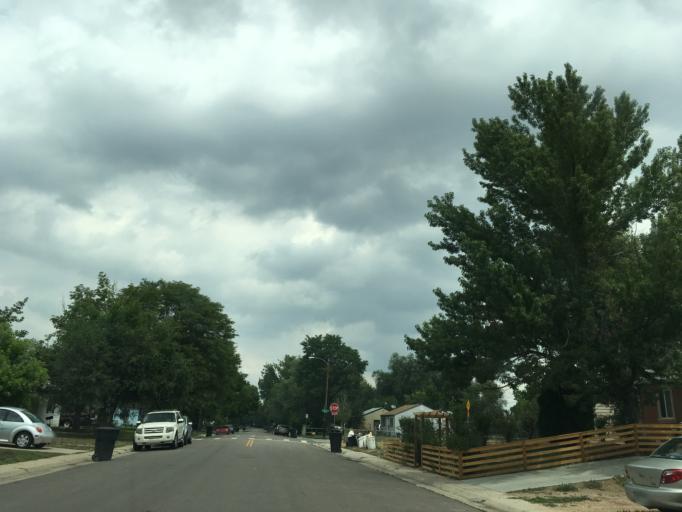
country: US
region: Colorado
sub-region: Arapahoe County
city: Sheridan
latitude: 39.6747
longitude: -105.0288
